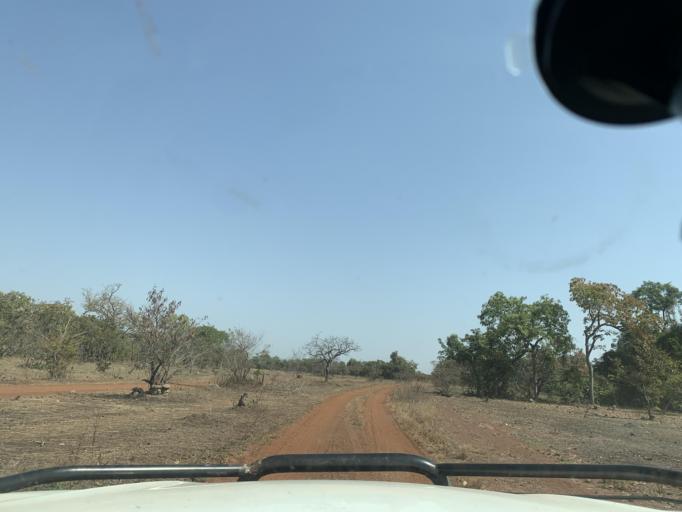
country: ML
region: Sikasso
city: Kolondieba
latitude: 10.8890
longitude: -6.7583
